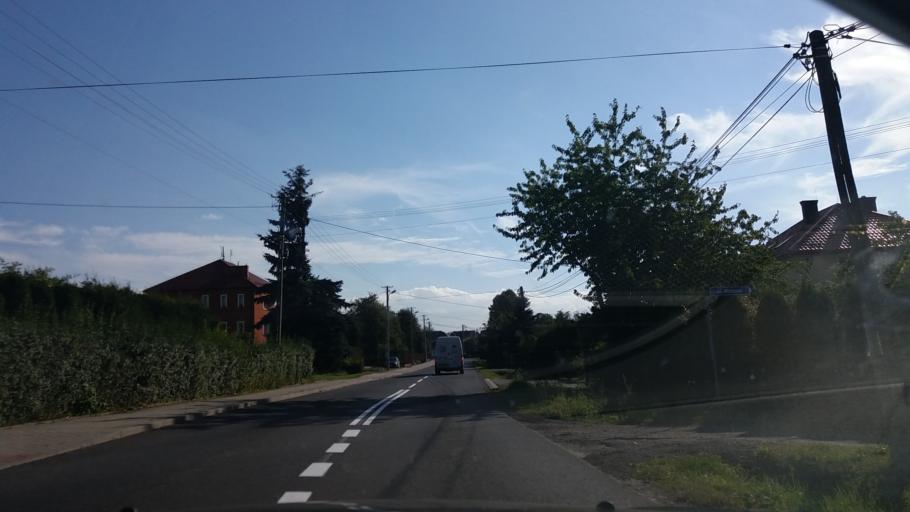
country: PL
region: Lesser Poland Voivodeship
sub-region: Powiat chrzanowski
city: Grojec
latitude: 50.0928
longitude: 19.5567
